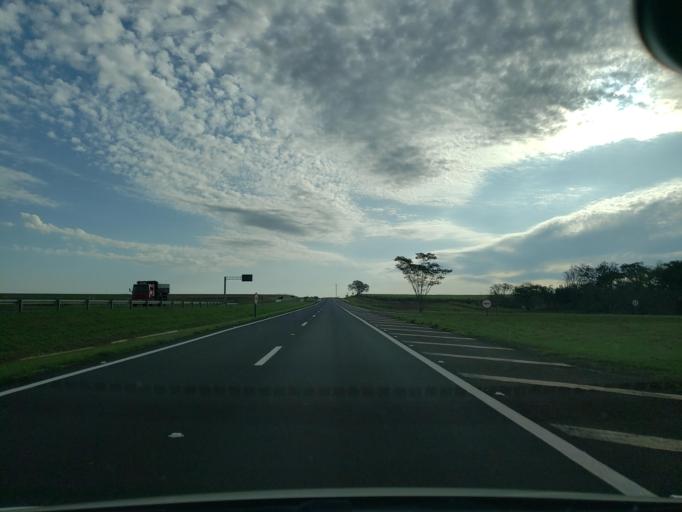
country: BR
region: Sao Paulo
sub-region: Valparaiso
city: Valparaiso
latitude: -21.2077
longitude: -50.7529
